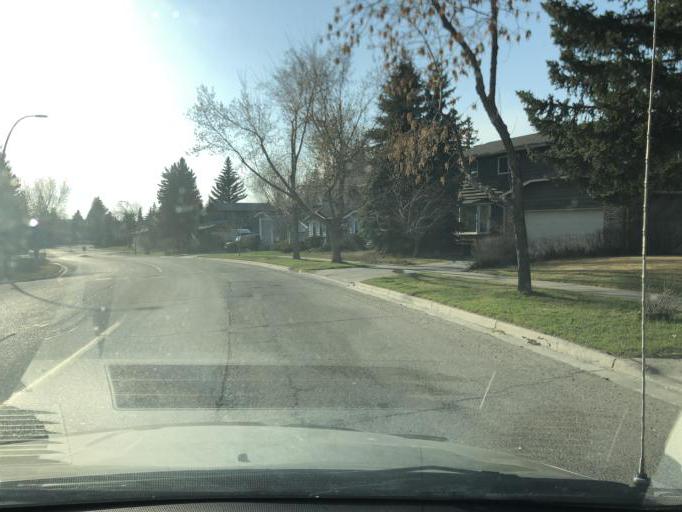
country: CA
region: Alberta
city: Calgary
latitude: 50.9666
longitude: -114.1047
